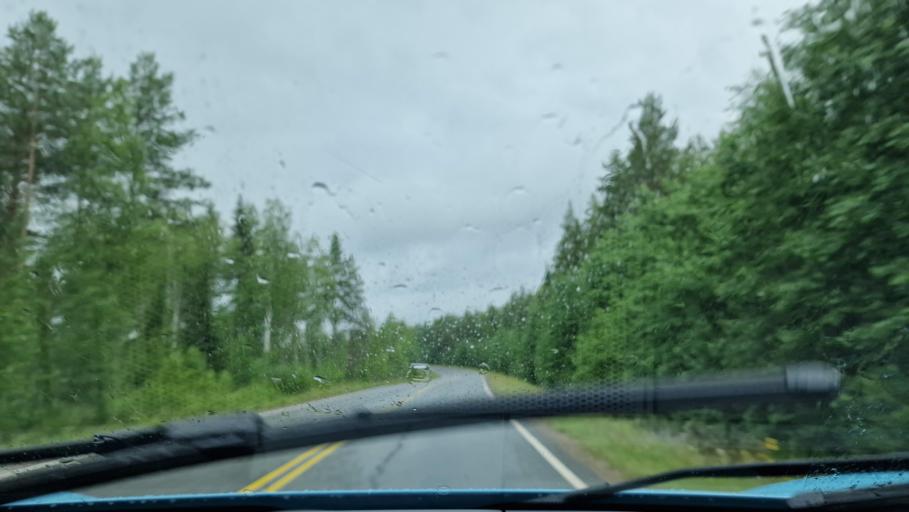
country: FI
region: Southern Ostrobothnia
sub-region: Jaerviseutu
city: Soini
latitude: 62.8079
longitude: 24.3615
